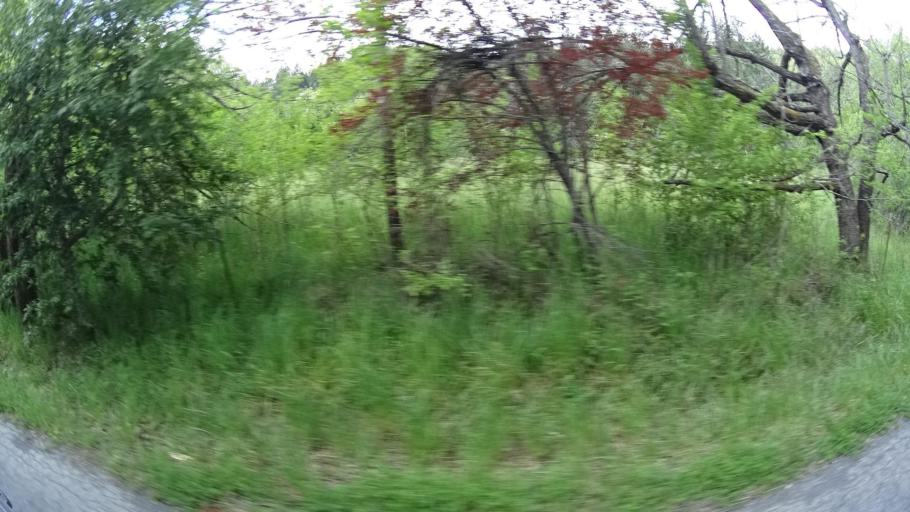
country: US
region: California
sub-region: Humboldt County
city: Redway
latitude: 40.0726
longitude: -123.8285
